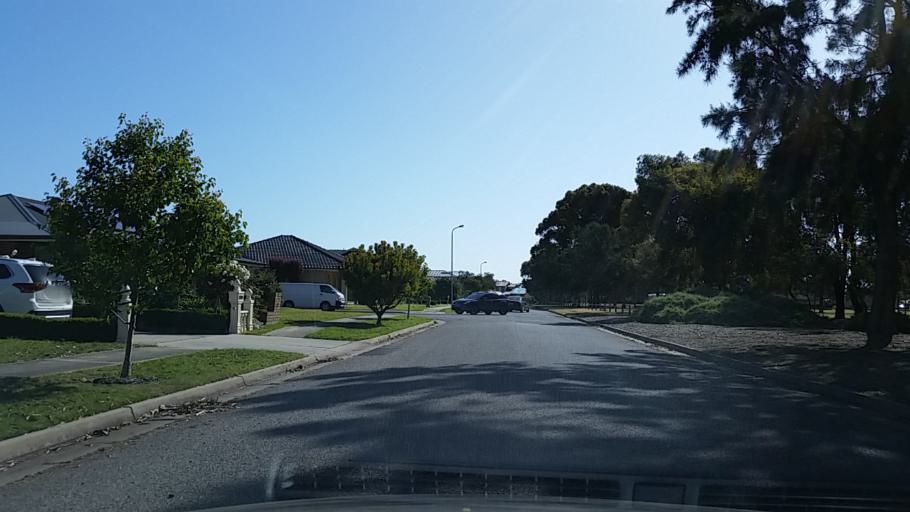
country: AU
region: South Australia
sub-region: Charles Sturt
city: Henley Beach
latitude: -34.9176
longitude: 138.5110
